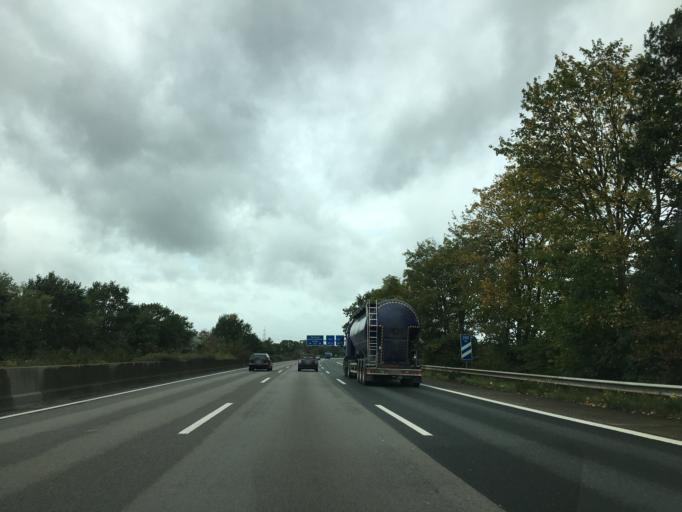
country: DE
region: North Rhine-Westphalia
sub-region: Regierungsbezirk Dusseldorf
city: Meerbusch
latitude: 51.2311
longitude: 6.6552
